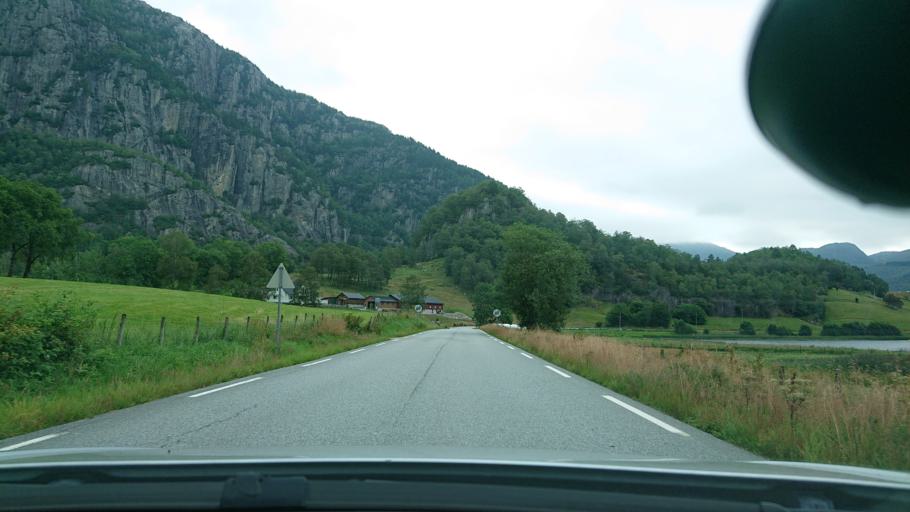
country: NO
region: Rogaland
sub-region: Hjelmeland
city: Hjelmelandsvagen
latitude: 59.2321
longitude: 6.1997
